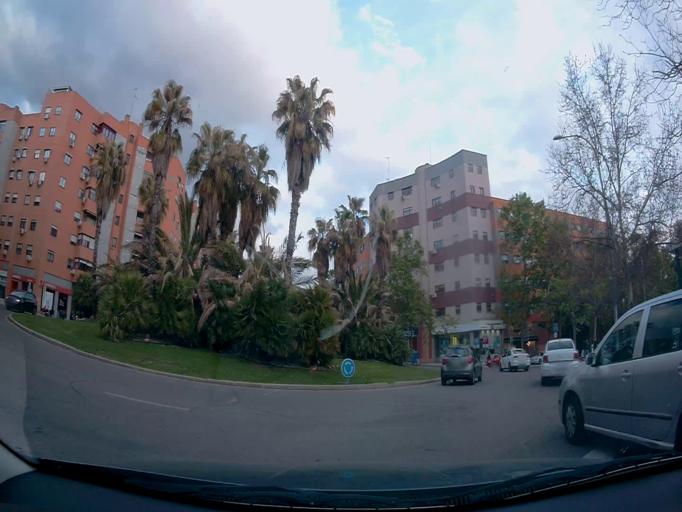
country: ES
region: Madrid
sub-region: Provincia de Madrid
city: Alcorcon
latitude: 40.3377
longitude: -3.8338
